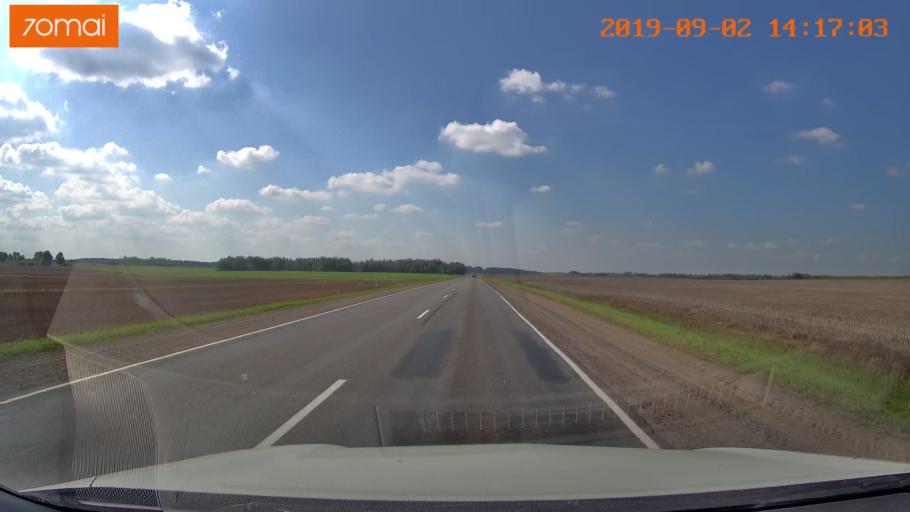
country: BY
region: Mogilev
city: Chavusy
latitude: 53.8122
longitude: 30.8177
